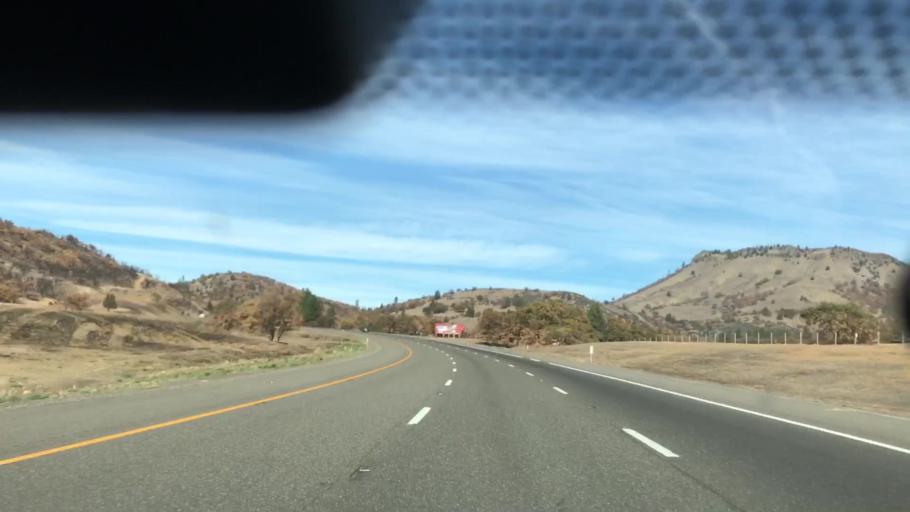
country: US
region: California
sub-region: Siskiyou County
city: Yreka
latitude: 41.9608
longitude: -122.5954
